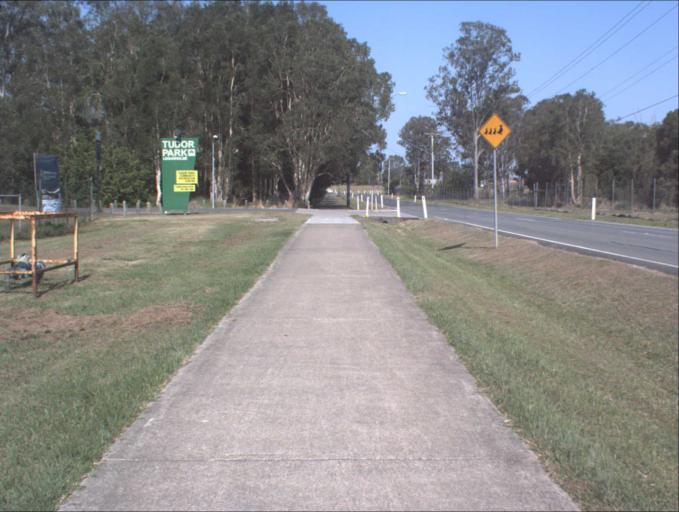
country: AU
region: Queensland
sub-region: Logan
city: Beenleigh
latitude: -27.6913
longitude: 153.1820
